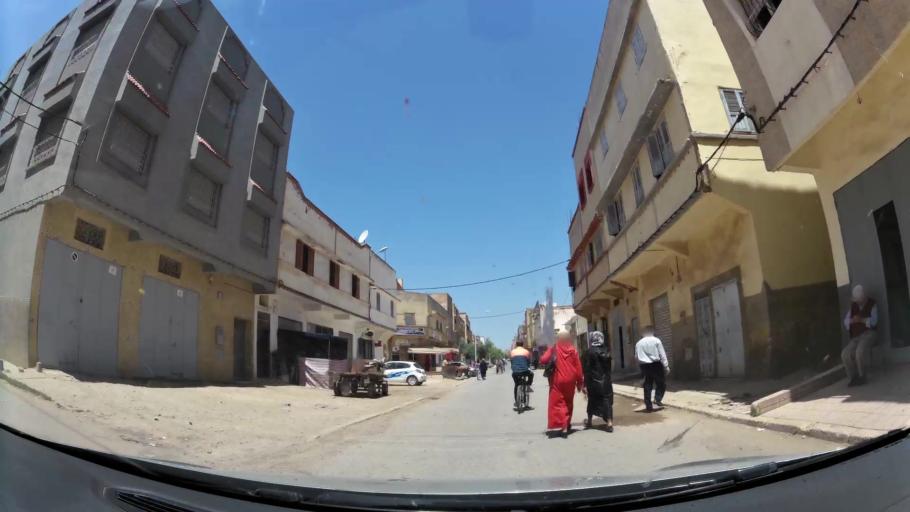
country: MA
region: Rabat-Sale-Zemmour-Zaer
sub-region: Khemisset
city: Khemisset
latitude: 33.8286
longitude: -6.0739
